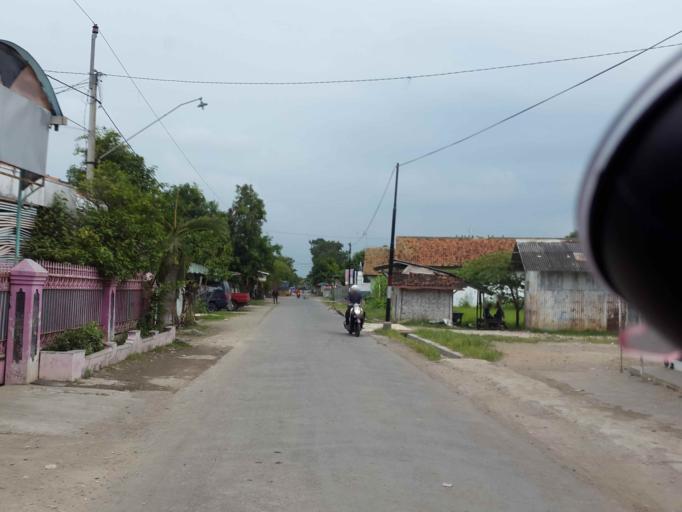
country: ID
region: Central Java
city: Pemalang
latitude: -6.8966
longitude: 109.3748
